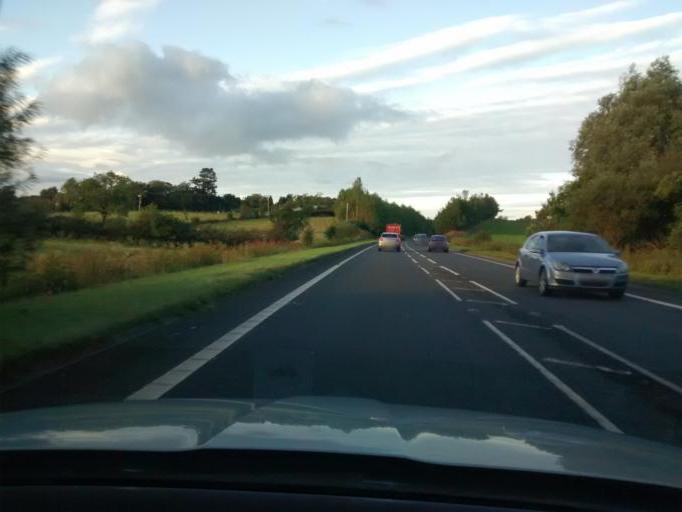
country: GB
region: Scotland
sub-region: Renfrewshire
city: Kilbarchan
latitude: 55.8239
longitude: -4.5417
